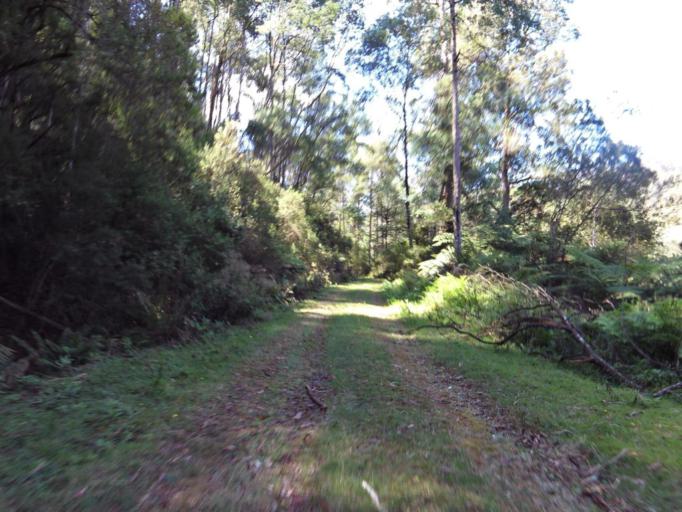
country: AU
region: Victoria
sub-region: Yarra Ranges
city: Millgrove
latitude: -37.6936
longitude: 145.8024
